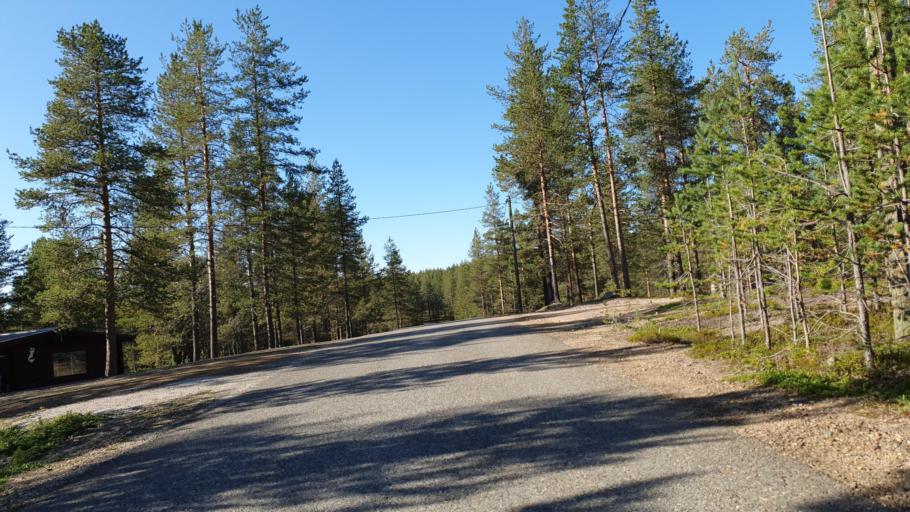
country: FI
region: Lapland
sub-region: Tunturi-Lappi
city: Kolari
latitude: 67.6074
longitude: 24.1953
